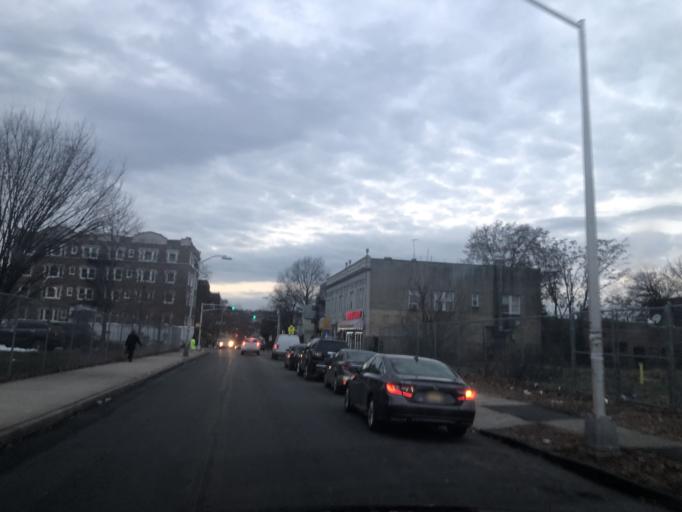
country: US
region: New Jersey
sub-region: Essex County
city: East Orange
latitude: 40.7646
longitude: -74.2106
